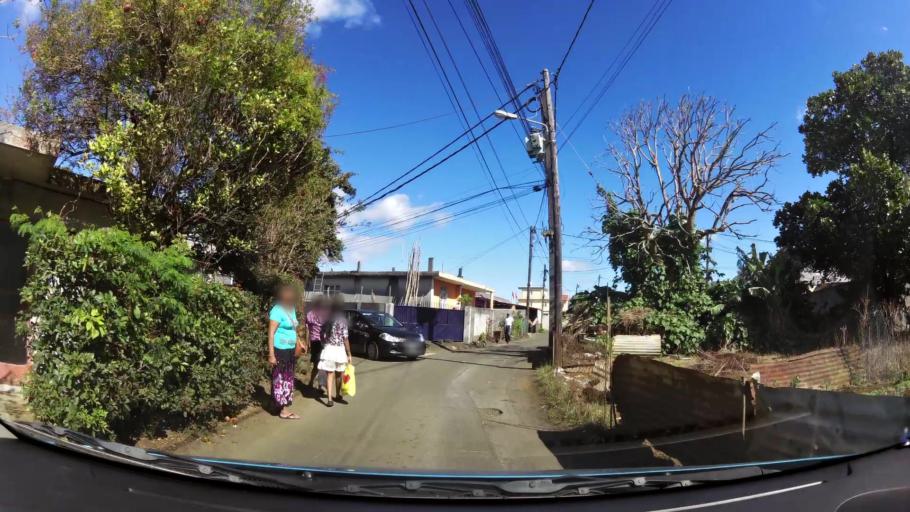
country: MU
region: Plaines Wilhems
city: Vacoas
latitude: -20.3167
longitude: 57.4898
